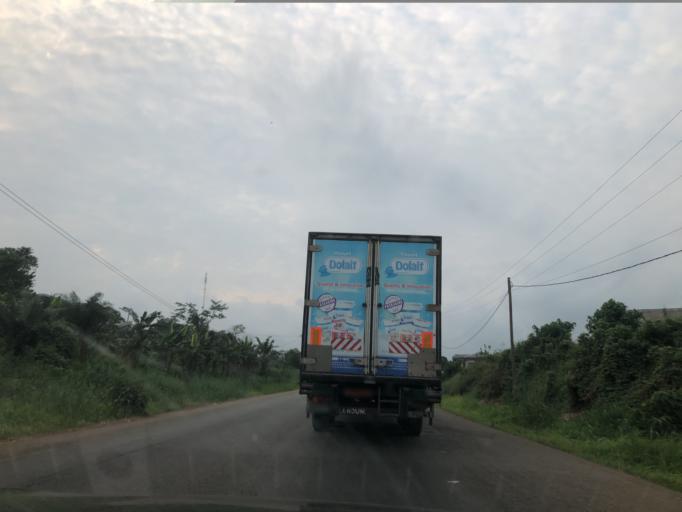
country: CM
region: Littoral
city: Edea
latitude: 3.8142
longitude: 10.1026
